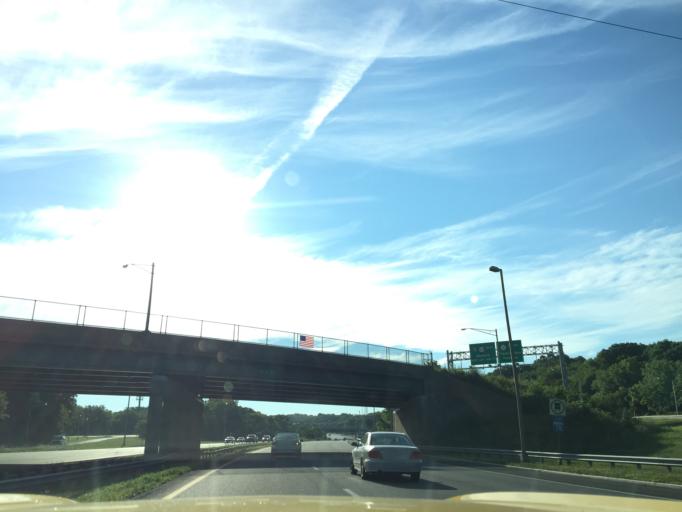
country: US
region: New Jersey
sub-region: Hunterdon County
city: Annandale
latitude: 40.6385
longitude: -74.8936
